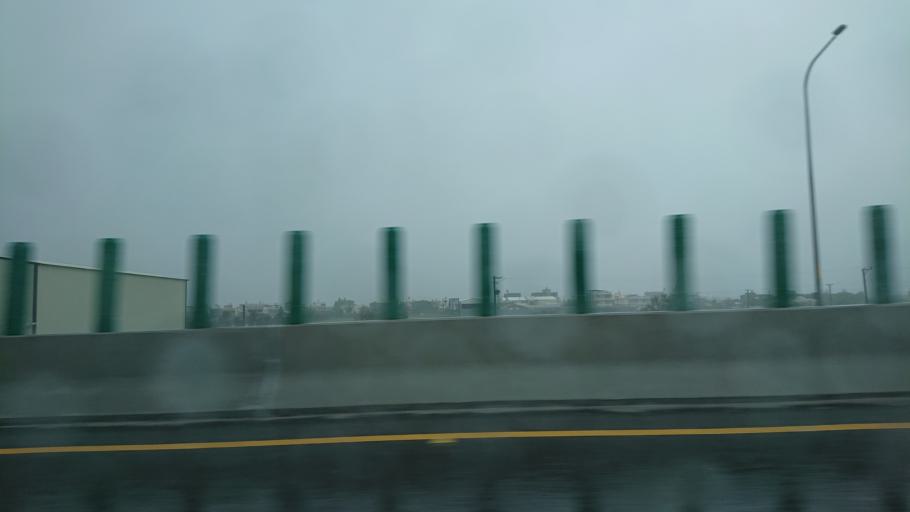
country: TW
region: Taiwan
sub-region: Changhua
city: Chang-hua
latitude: 23.9421
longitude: 120.3237
